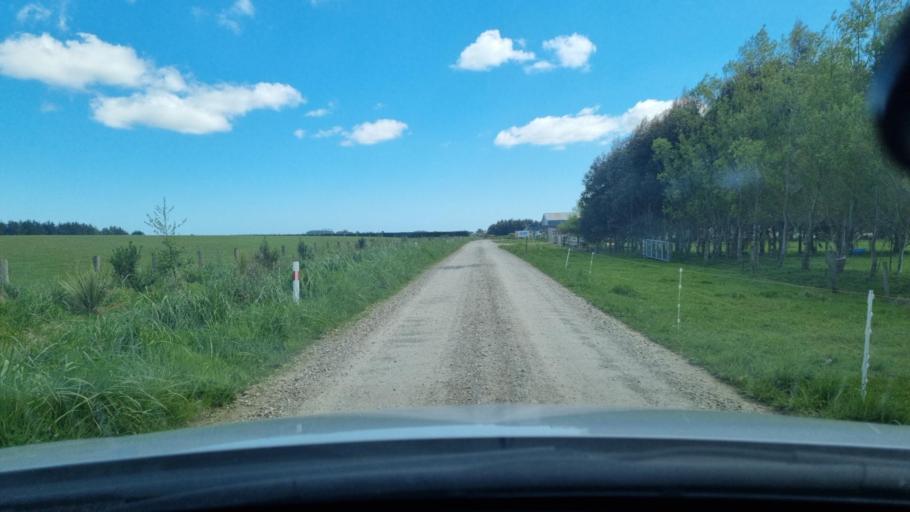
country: NZ
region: Southland
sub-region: Invercargill City
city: Invercargill
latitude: -46.3740
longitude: 168.3404
